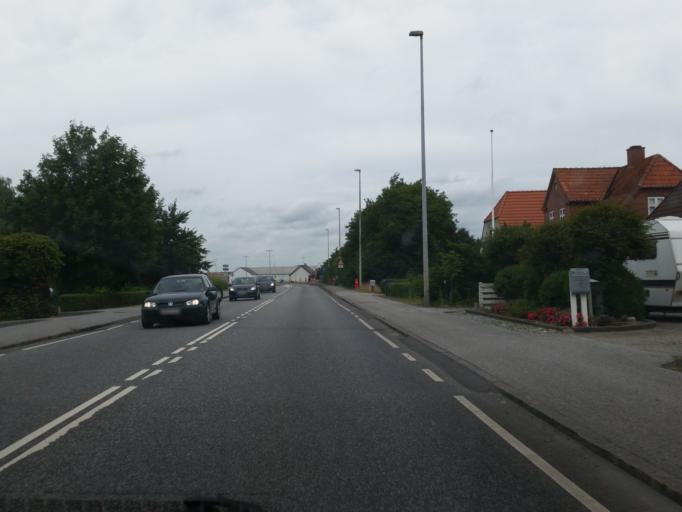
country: DK
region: South Denmark
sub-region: Esbjerg Kommune
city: Ribe
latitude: 55.3480
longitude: 8.7793
